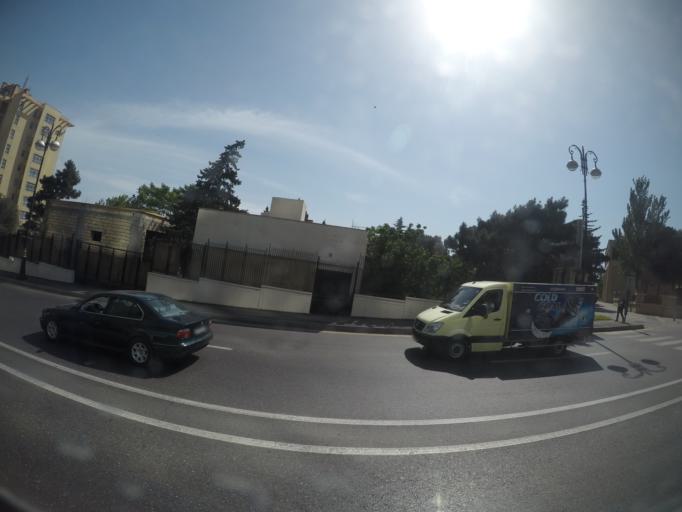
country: AZ
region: Baki
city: Badamdar
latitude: 40.3595
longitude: 49.8275
